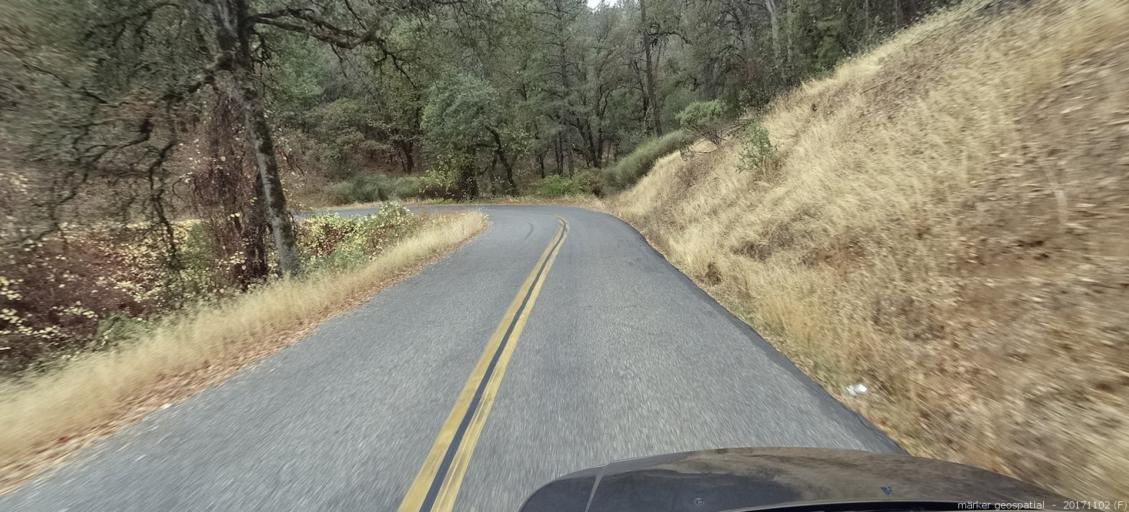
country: US
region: California
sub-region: Shasta County
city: Bella Vista
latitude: 40.7419
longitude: -122.2400
